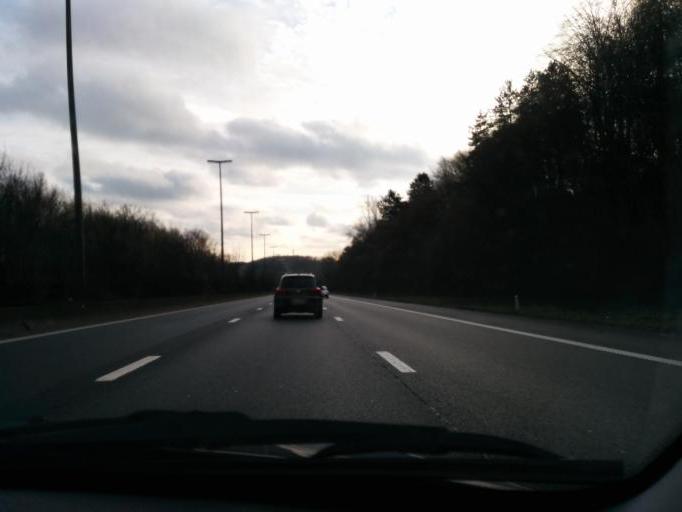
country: BE
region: Flanders
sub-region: Provincie Vlaams-Brabant
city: Hoeilaart
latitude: 50.7744
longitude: 4.5007
